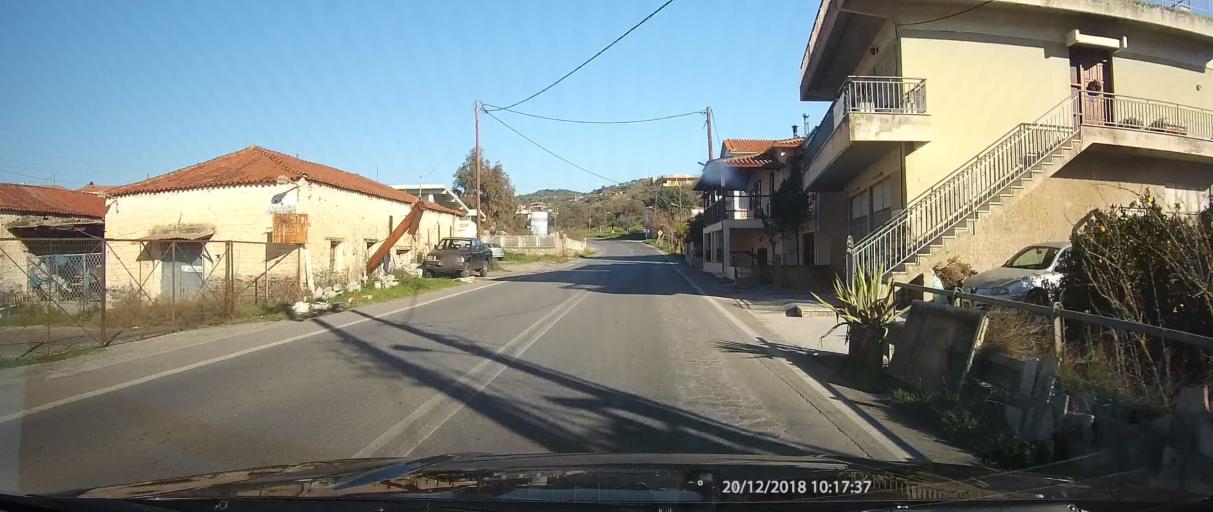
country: GR
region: Peloponnese
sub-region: Nomos Lakonias
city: Sparti
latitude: 37.1088
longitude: 22.4336
